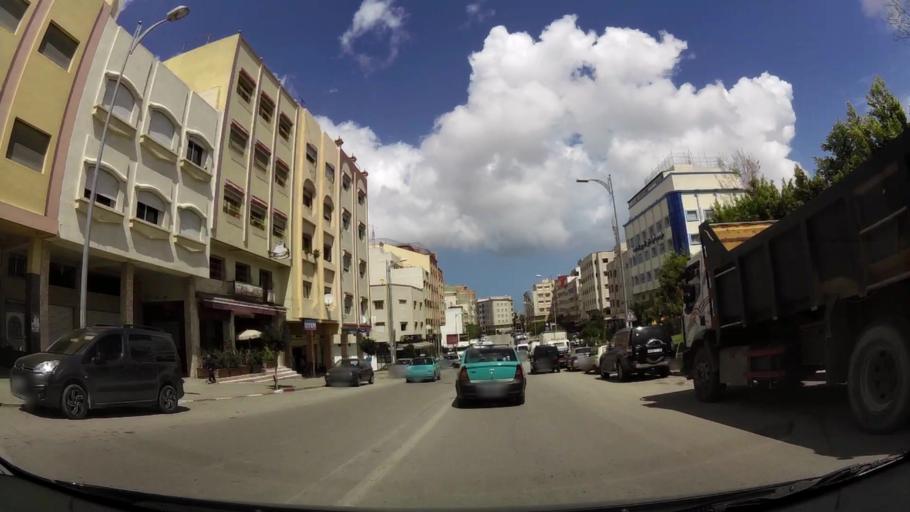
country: MA
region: Tanger-Tetouan
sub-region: Tanger-Assilah
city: Tangier
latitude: 35.7516
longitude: -5.8290
